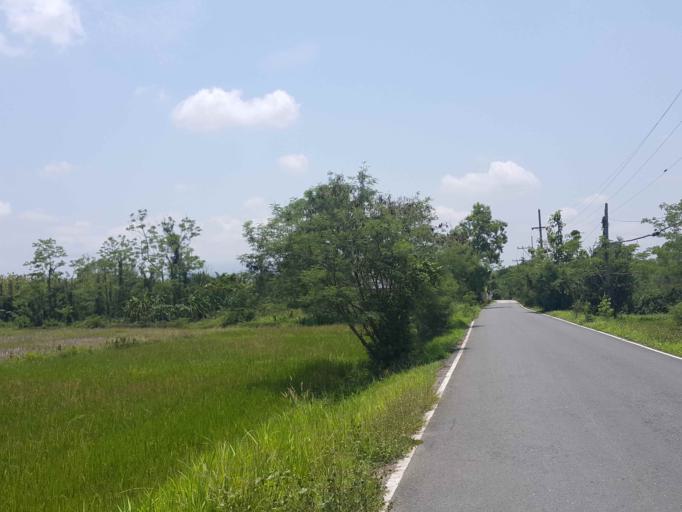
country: TH
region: Chiang Mai
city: San Sai
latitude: 18.8072
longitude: 99.0845
